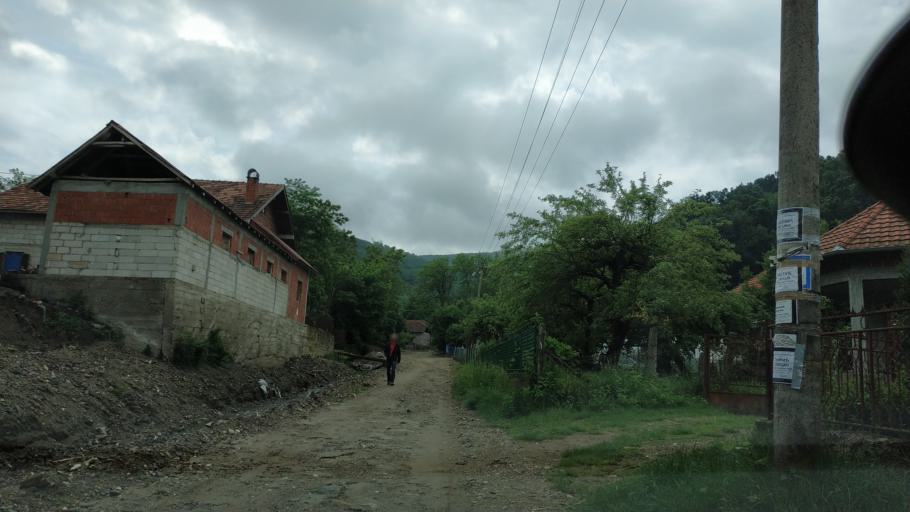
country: RS
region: Central Serbia
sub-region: Nisavski Okrug
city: Aleksinac
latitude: 43.4285
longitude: 21.6522
